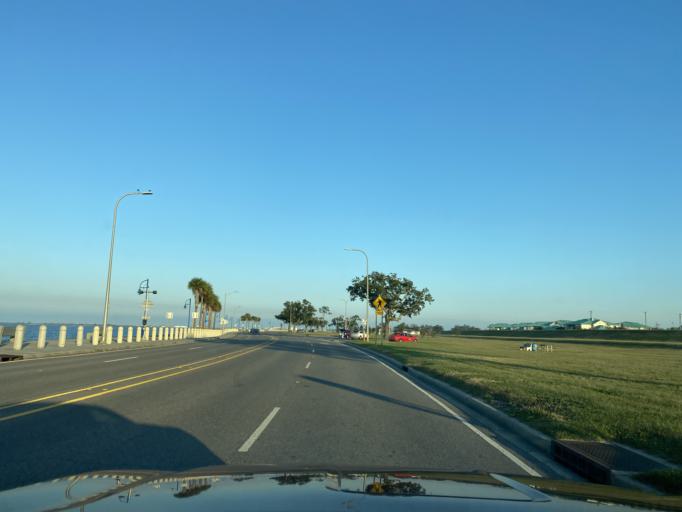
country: US
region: Louisiana
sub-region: Orleans Parish
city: New Orleans
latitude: 30.0347
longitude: -90.0492
